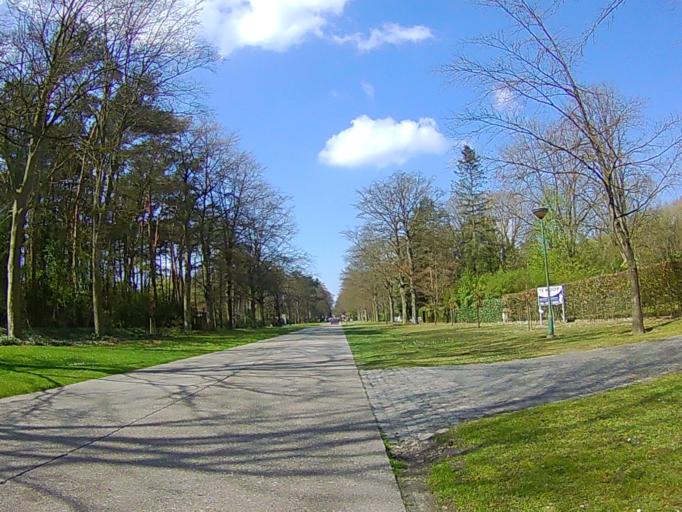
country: BE
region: Flanders
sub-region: Provincie Antwerpen
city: Schilde
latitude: 51.2248
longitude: 4.5533
